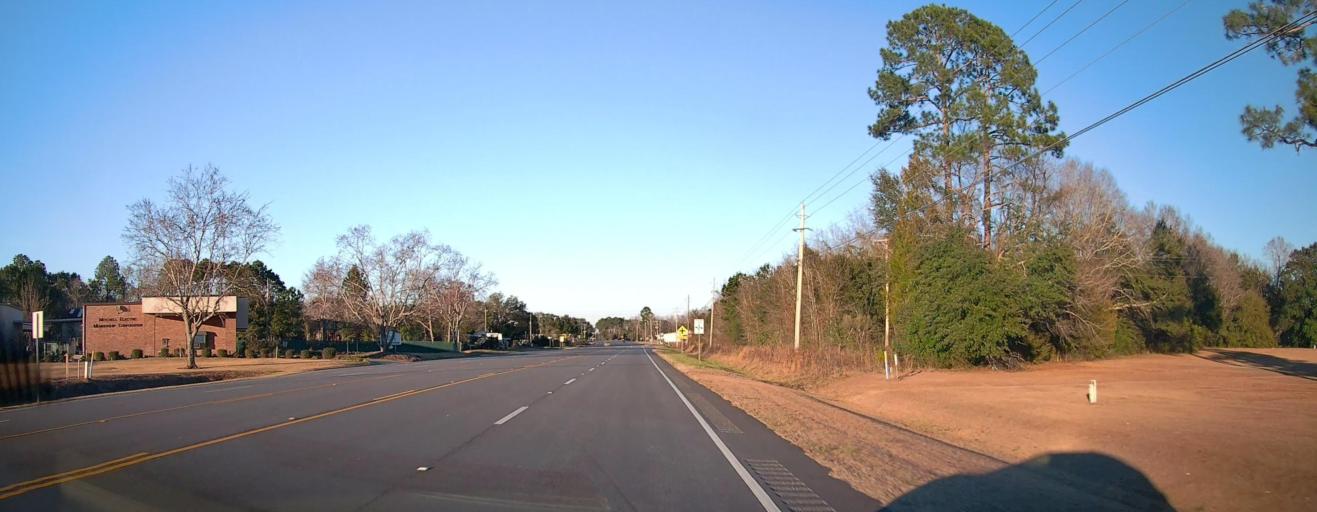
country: US
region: Georgia
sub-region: Dougherty County
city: Albany
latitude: 31.5114
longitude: -84.2035
